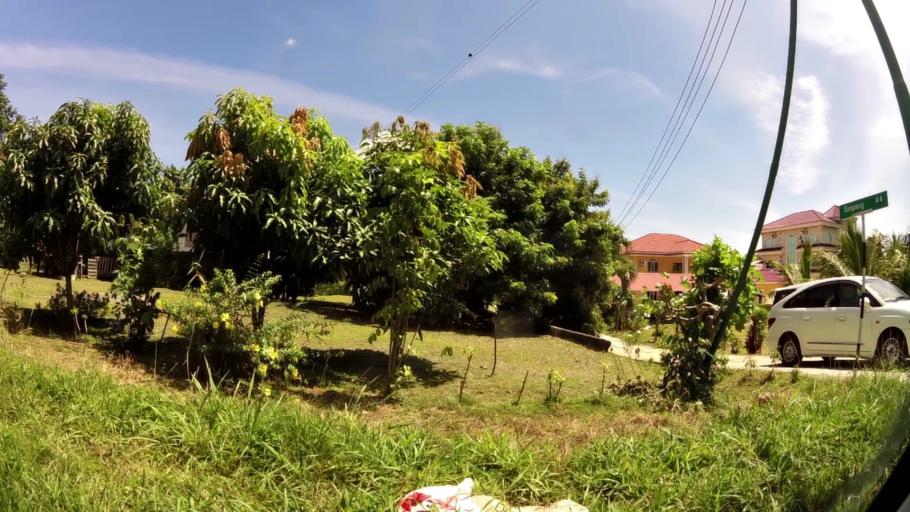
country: BN
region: Brunei and Muara
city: Bandar Seri Begawan
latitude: 4.9343
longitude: 114.9545
